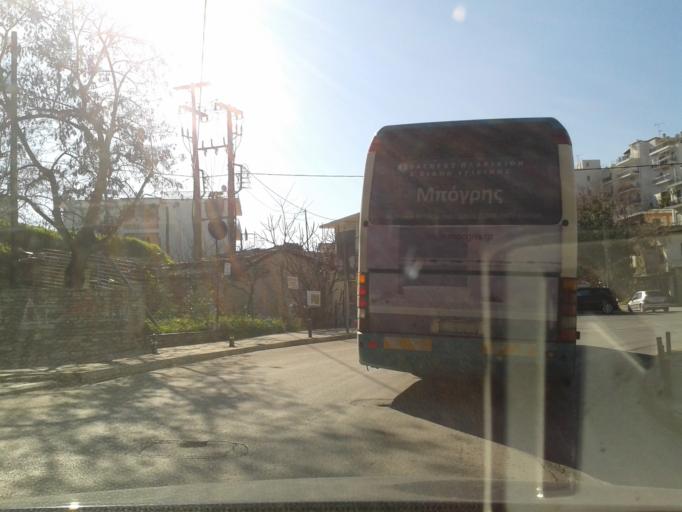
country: GR
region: Central Greece
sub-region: Nomos Voiotias
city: Thivai
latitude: 38.3214
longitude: 23.3206
